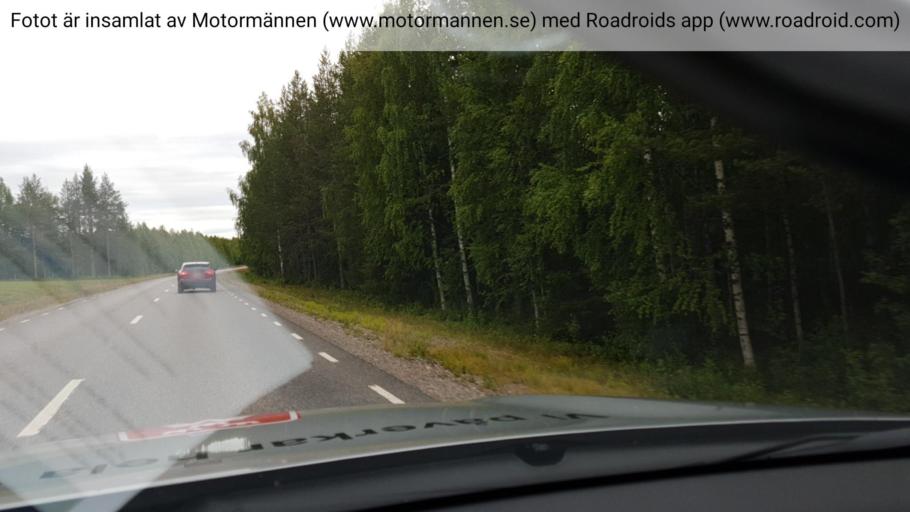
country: SE
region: Norrbotten
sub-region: Overkalix Kommun
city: OEverkalix
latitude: 66.5811
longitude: 22.7581
